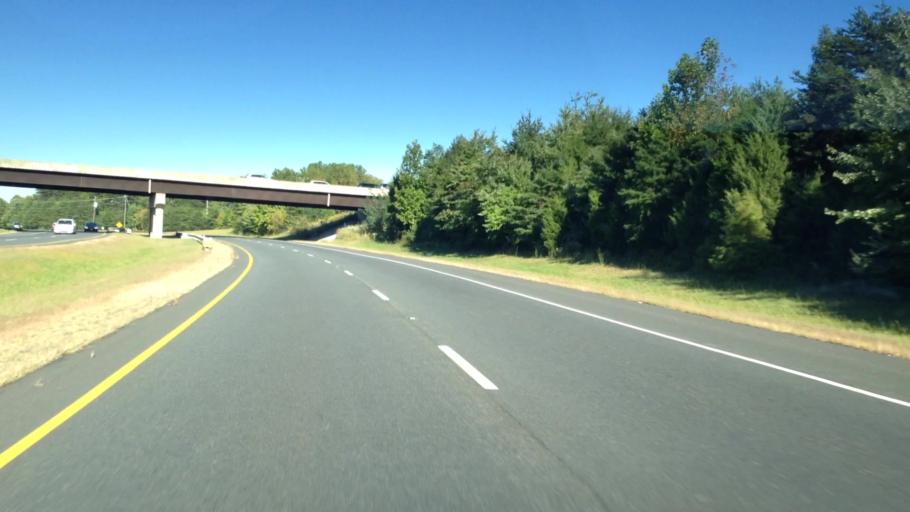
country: US
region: Virginia
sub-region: Fairfax County
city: West Springfield
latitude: 38.7456
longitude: -77.2500
